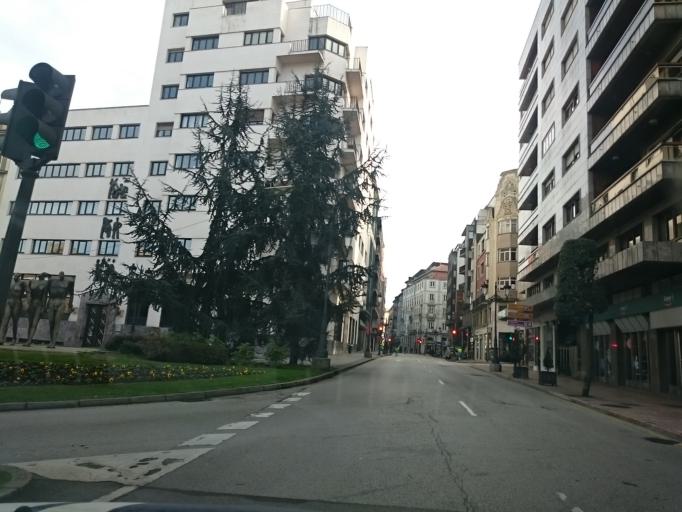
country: ES
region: Asturias
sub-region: Province of Asturias
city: Oviedo
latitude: 43.3637
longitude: -5.8428
